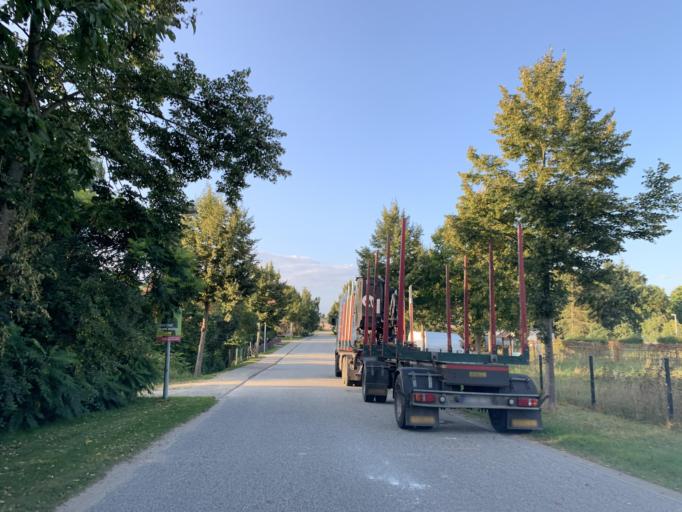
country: DE
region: Mecklenburg-Vorpommern
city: Loitz
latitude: 53.3658
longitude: 13.4433
